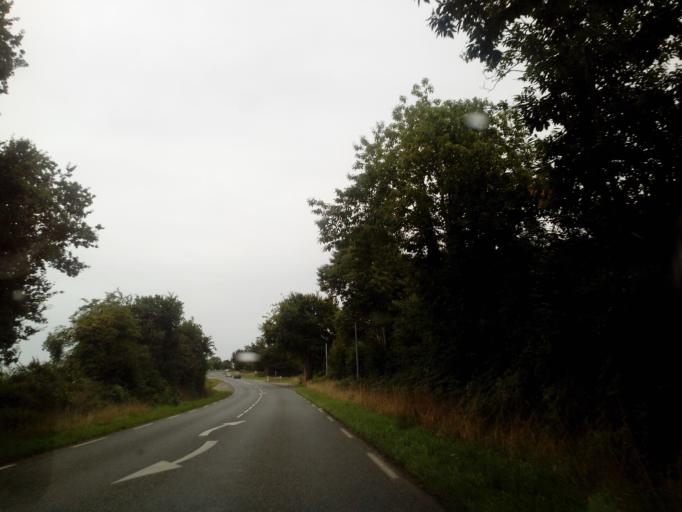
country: FR
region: Brittany
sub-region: Departement du Finistere
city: Quimperle
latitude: 47.8538
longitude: -3.5121
